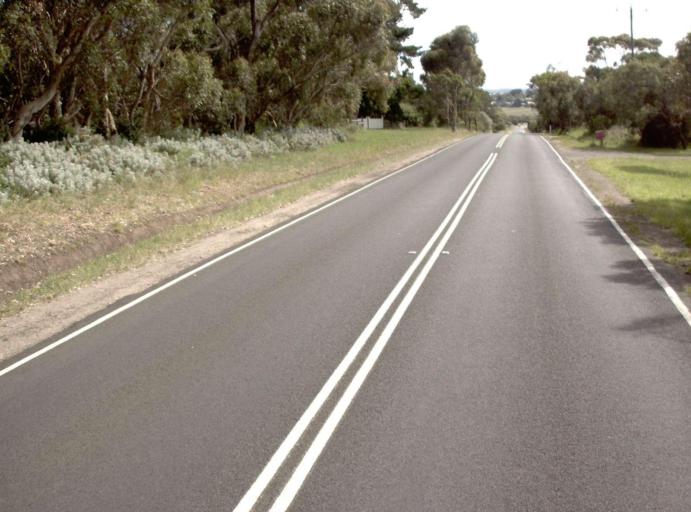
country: AU
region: Victoria
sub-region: Bass Coast
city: Phillip Island
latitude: -38.4701
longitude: 145.1900
